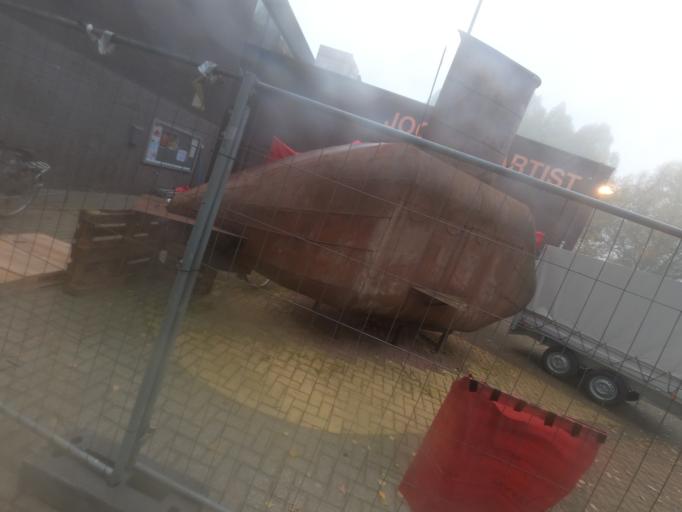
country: BE
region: Flanders
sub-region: Provincie Oost-Vlaanderen
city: Temse
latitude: 51.1290
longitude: 4.2045
